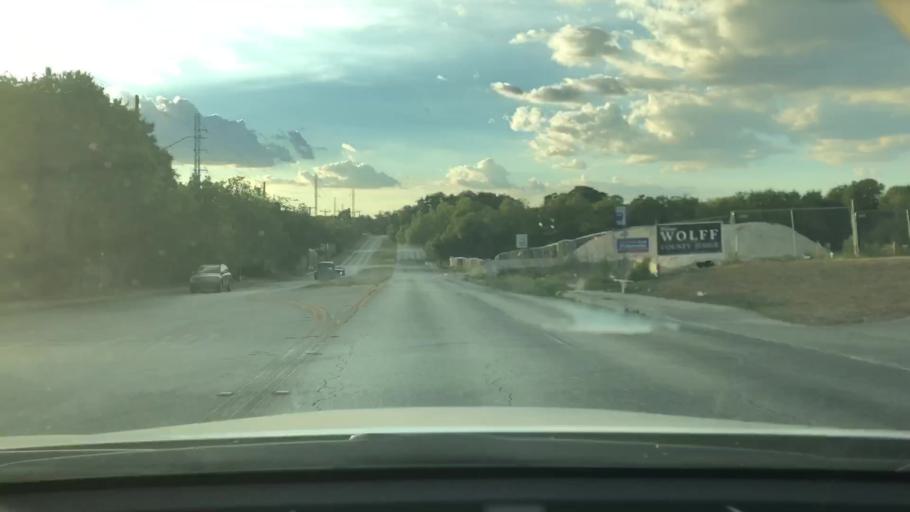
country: US
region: Texas
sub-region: Bexar County
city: Hollywood Park
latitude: 29.5531
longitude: -98.4684
